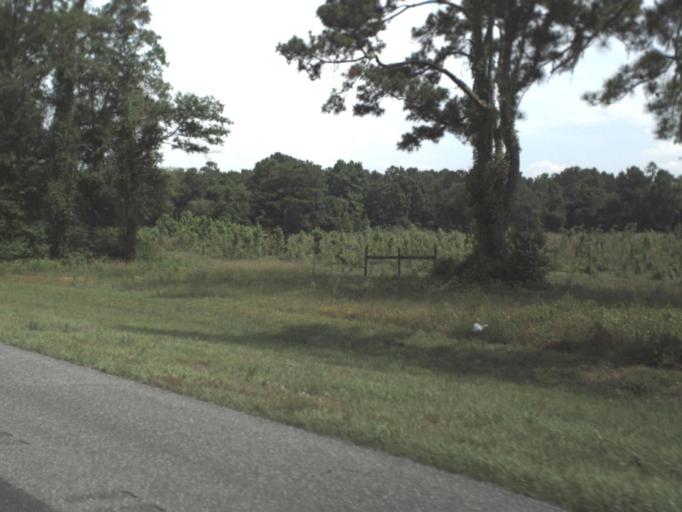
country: US
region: Florida
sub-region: Suwannee County
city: Wellborn
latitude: 30.2909
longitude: -82.8723
